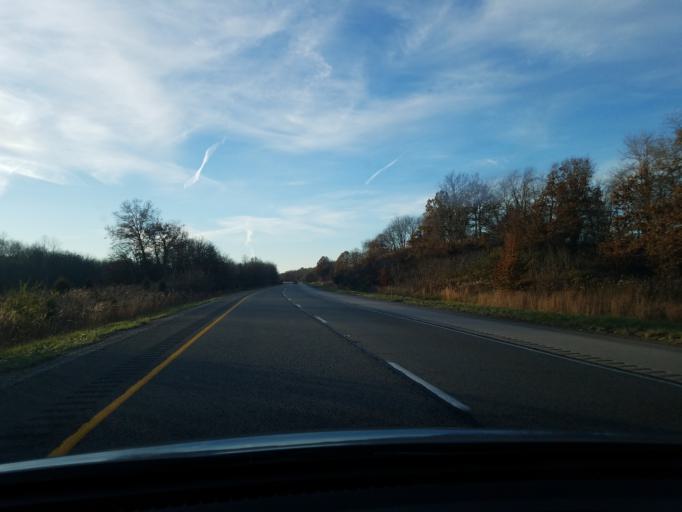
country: US
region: Indiana
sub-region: Spencer County
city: Dale
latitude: 38.1971
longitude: -87.1432
